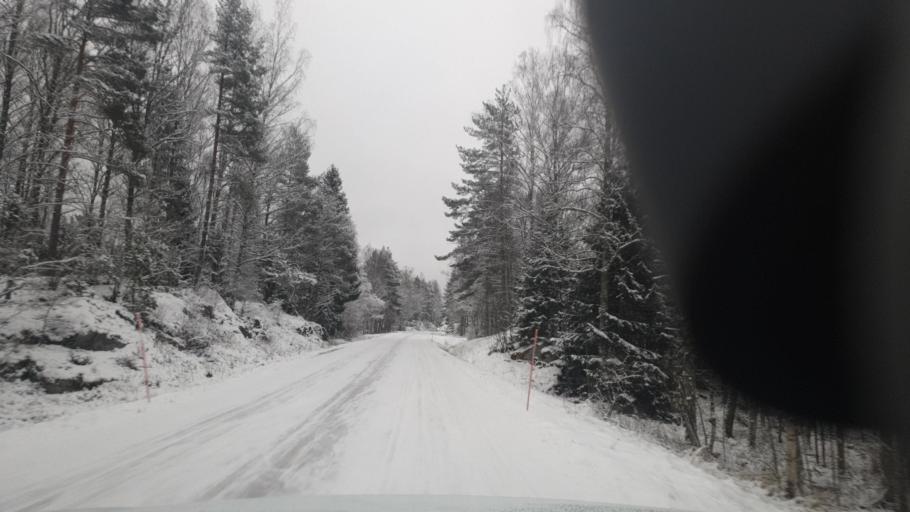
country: NO
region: Hedmark
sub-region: Eidskog
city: Skotterud
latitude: 59.7897
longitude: 12.0310
